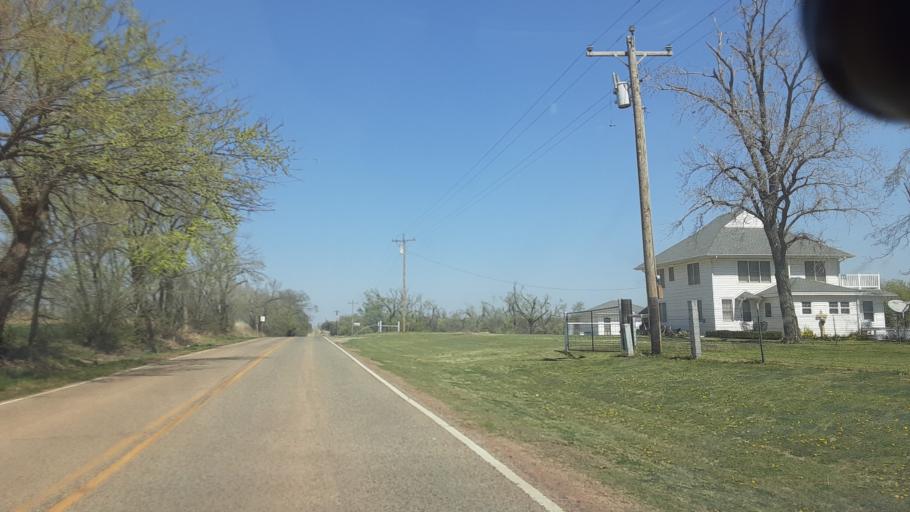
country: US
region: Oklahoma
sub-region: Logan County
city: Guthrie
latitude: 35.8168
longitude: -97.4783
